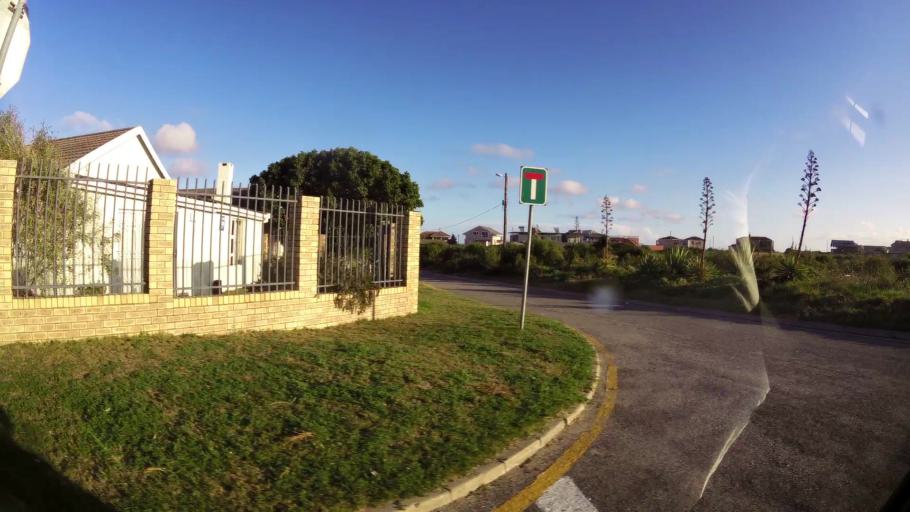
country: ZA
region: Western Cape
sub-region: Eden District Municipality
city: George
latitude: -34.0030
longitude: 22.6542
